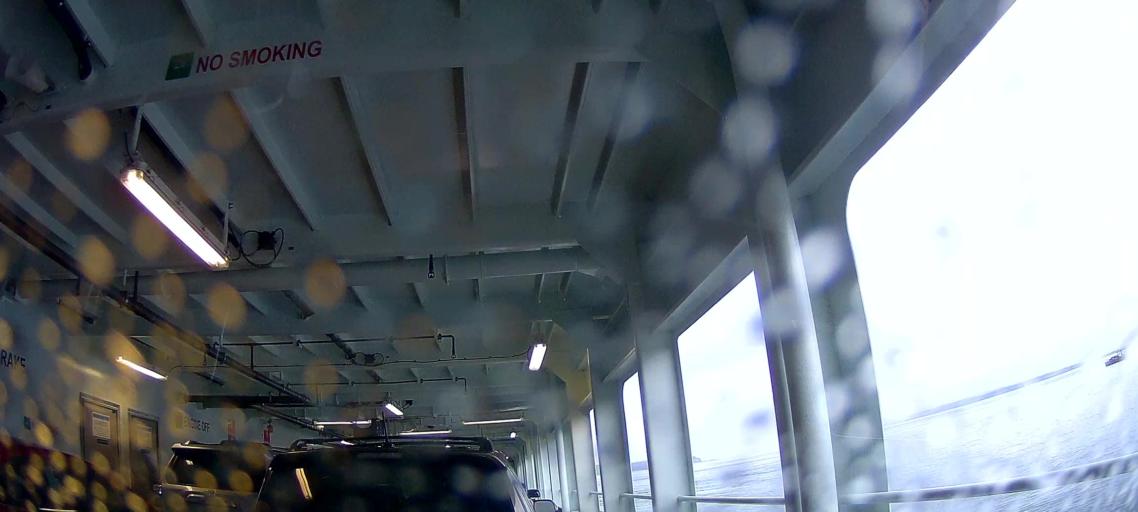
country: US
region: Washington
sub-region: Snohomish County
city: Mukilteo
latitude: 47.9511
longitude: -122.2965
